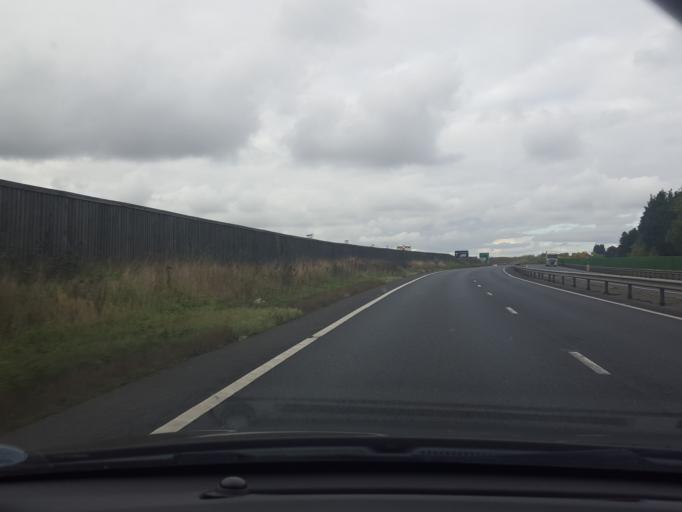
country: GB
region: England
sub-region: Suffolk
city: Stowmarket
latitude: 52.1997
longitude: 0.9854
